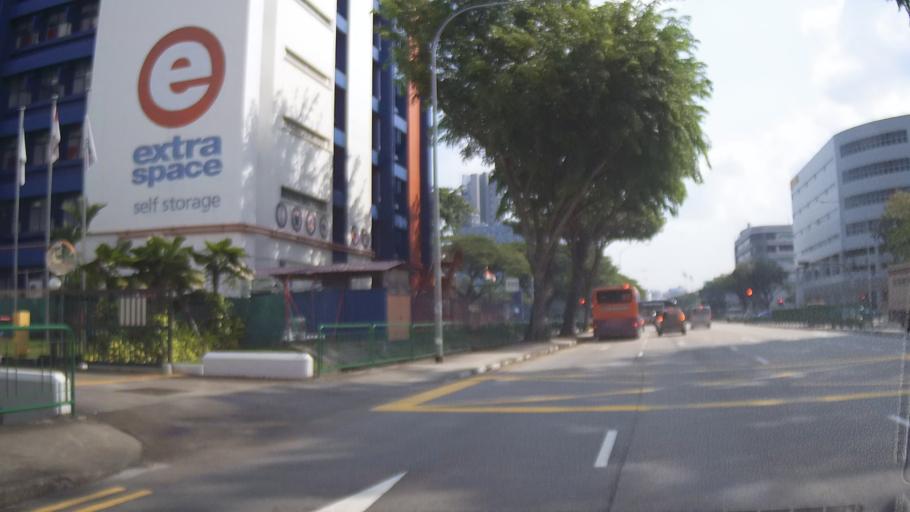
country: SG
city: Singapore
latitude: 1.3164
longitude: 103.8646
